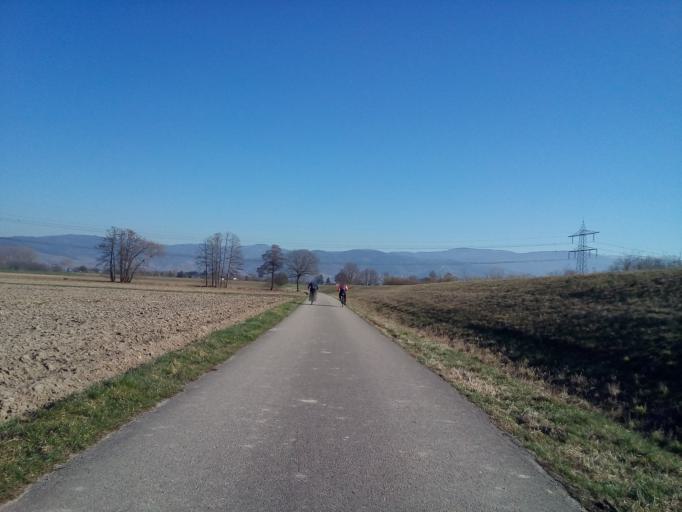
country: DE
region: Baden-Wuerttemberg
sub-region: Karlsruhe Region
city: Zell
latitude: 48.7037
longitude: 8.0949
